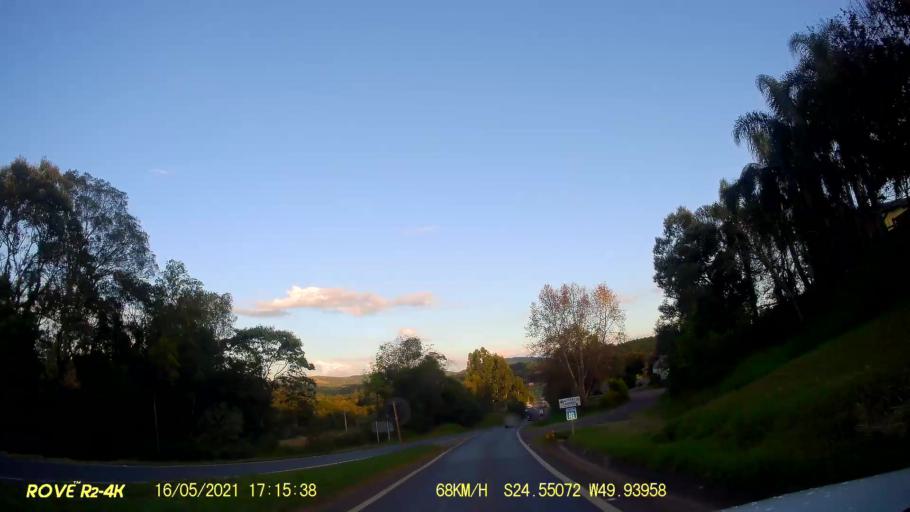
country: BR
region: Parana
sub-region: Pirai Do Sul
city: Pirai do Sul
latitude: -24.5508
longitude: -49.9395
